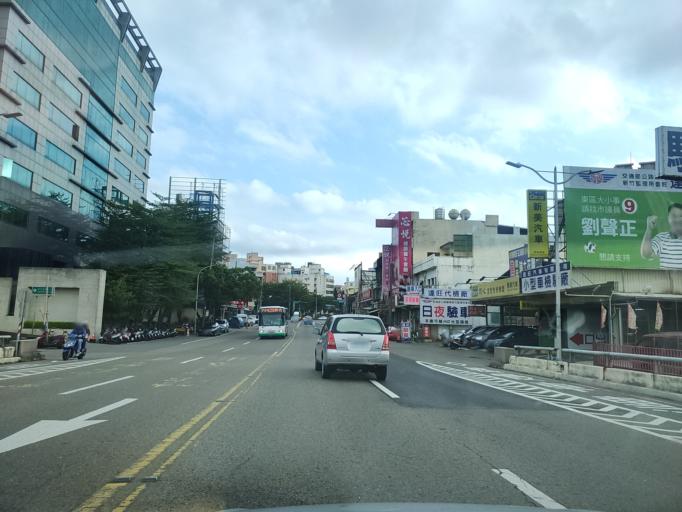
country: TW
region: Taiwan
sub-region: Hsinchu
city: Hsinchu
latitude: 24.8067
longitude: 120.9857
